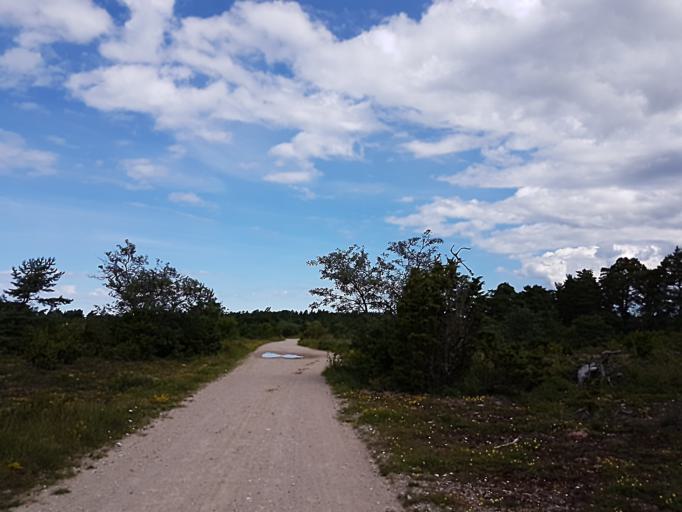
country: SE
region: Gotland
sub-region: Gotland
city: Visby
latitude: 57.6083
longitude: 18.3223
